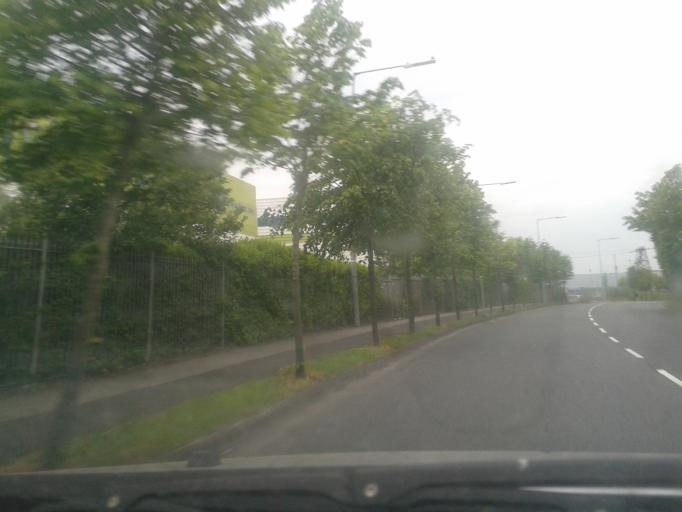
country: IE
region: Leinster
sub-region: Dublin City
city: Finglas
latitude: 53.4000
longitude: -6.2941
